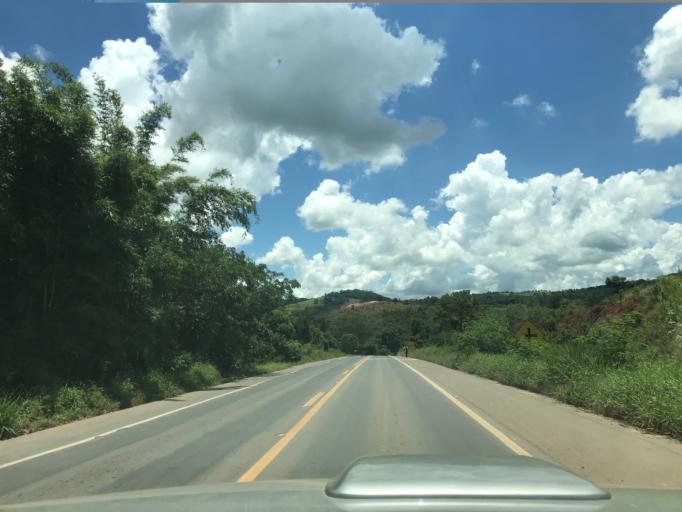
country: BR
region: Minas Gerais
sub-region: Perdoes
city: Perdoes
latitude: -21.0988
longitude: -45.0994
